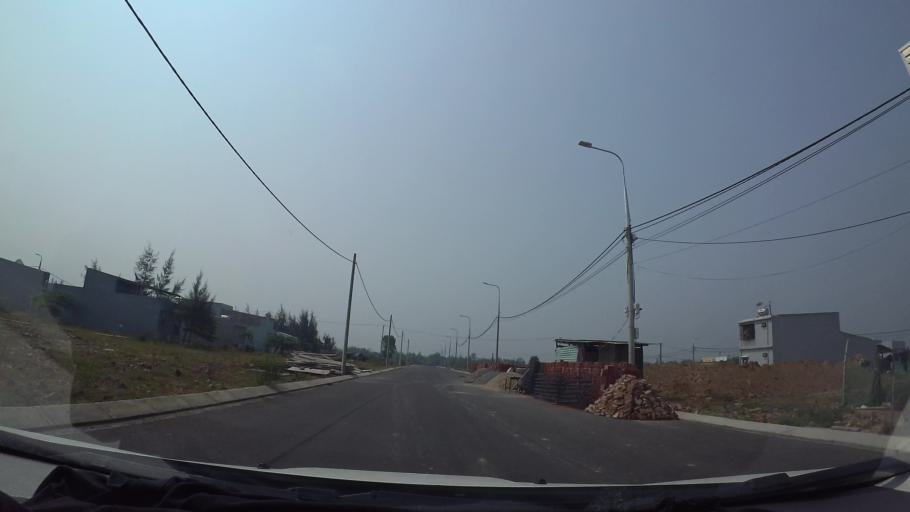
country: VN
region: Da Nang
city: Cam Le
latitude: 15.9830
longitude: 108.2275
